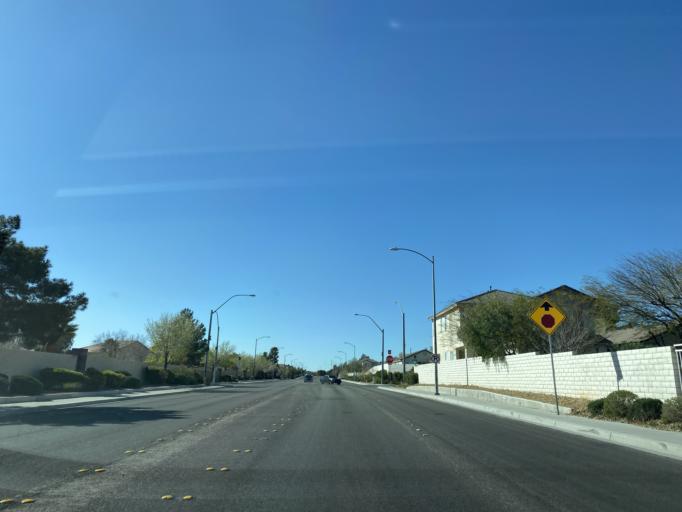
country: US
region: Nevada
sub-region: Clark County
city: Summerlin South
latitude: 36.3111
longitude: -115.2877
